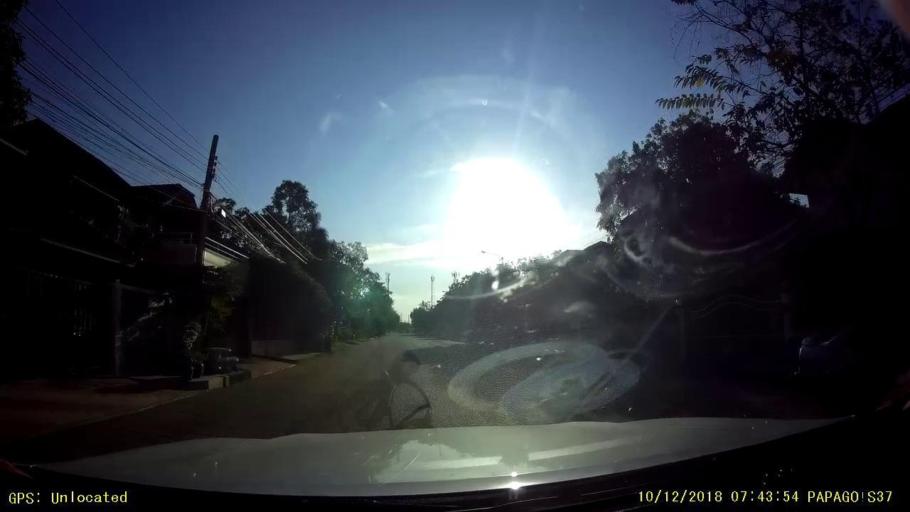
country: TH
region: Bangkok
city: Lat Krabang
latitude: 13.7913
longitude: 100.8159
